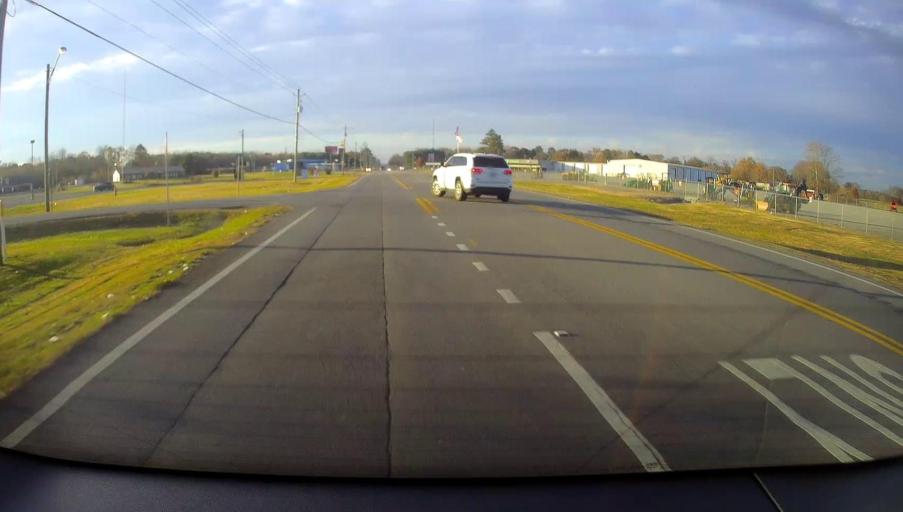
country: US
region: Alabama
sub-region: Blount County
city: Oneonta
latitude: 34.1171
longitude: -86.3912
